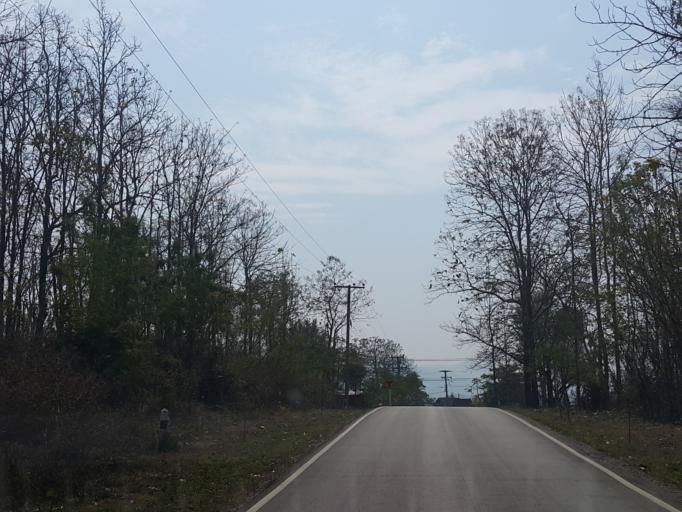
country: TH
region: Chiang Mai
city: Mae On
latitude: 18.8141
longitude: 99.2511
